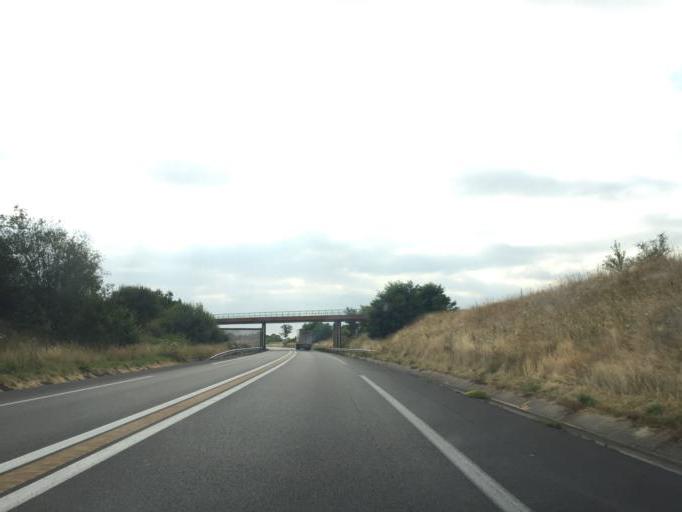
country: FR
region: Auvergne
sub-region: Departement de l'Allier
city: Saint-Francois
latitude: 46.4723
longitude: 3.8672
